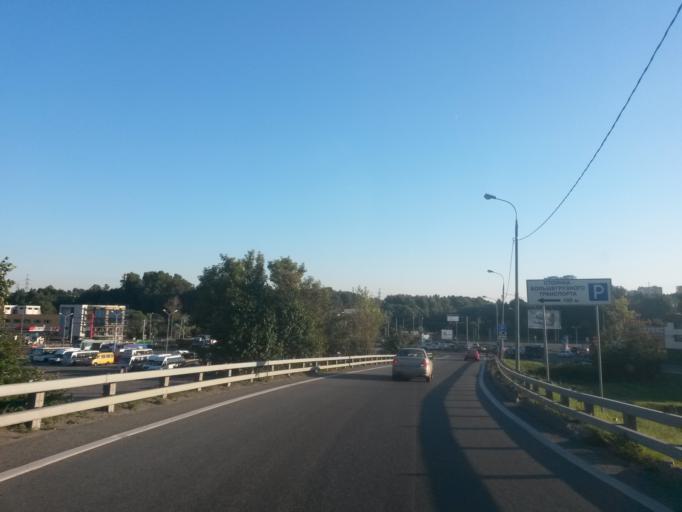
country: RU
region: Moscow
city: Annino
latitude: 55.5691
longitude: 37.5987
